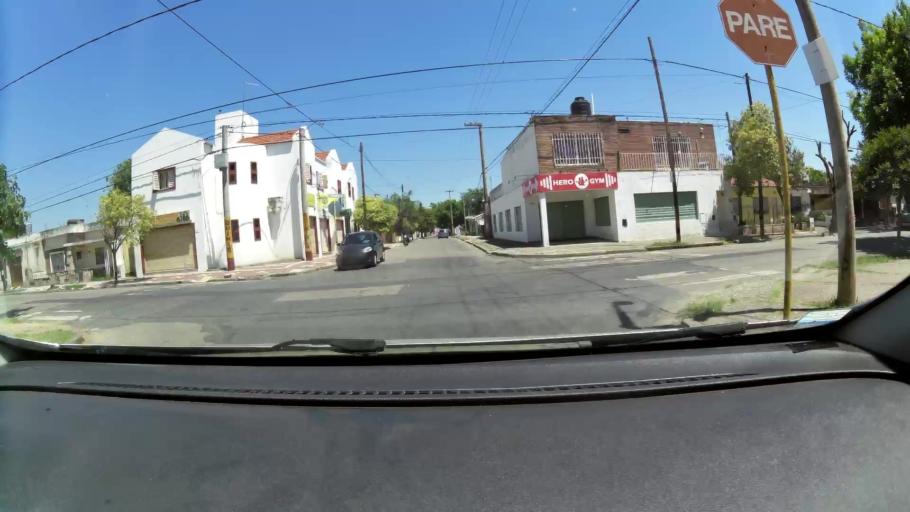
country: AR
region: Cordoba
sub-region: Departamento de Capital
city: Cordoba
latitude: -31.4183
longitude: -64.2297
